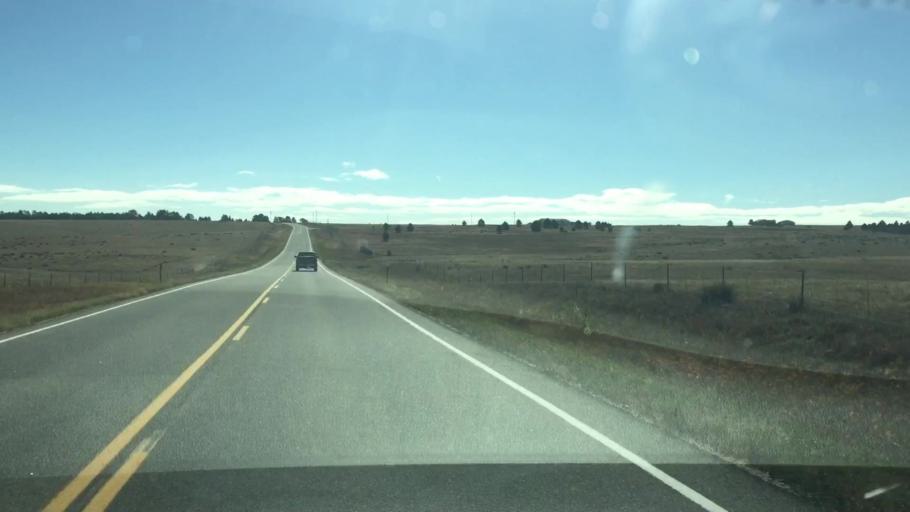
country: US
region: Colorado
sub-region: Elbert County
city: Kiowa
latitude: 39.3357
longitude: -104.4249
